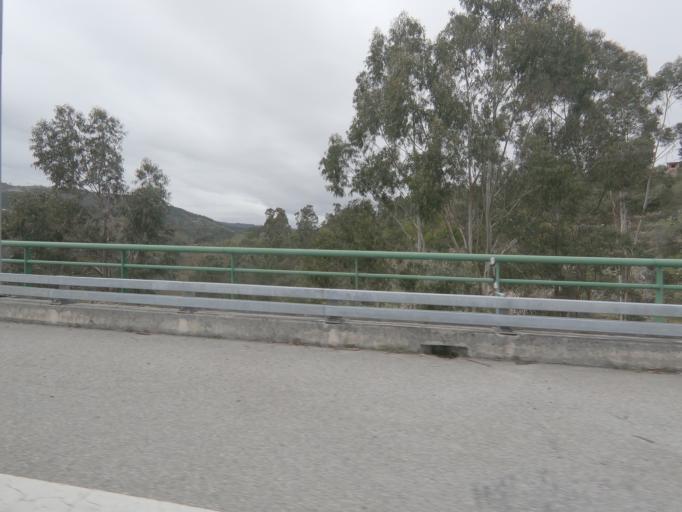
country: PT
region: Viseu
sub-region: Castro Daire
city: Castro Daire
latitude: 40.8953
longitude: -7.9239
